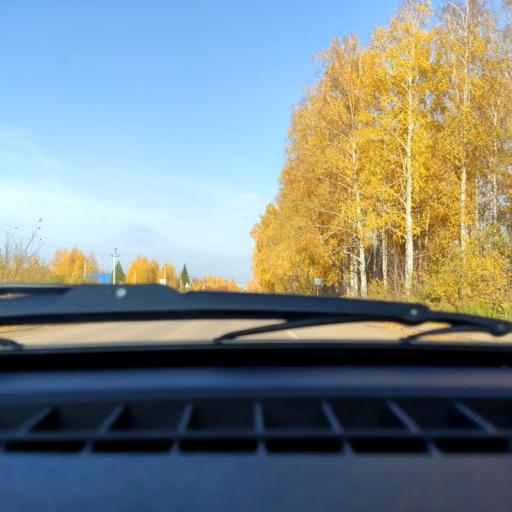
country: RU
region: Bashkortostan
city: Kabakovo
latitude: 54.7058
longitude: 56.1702
